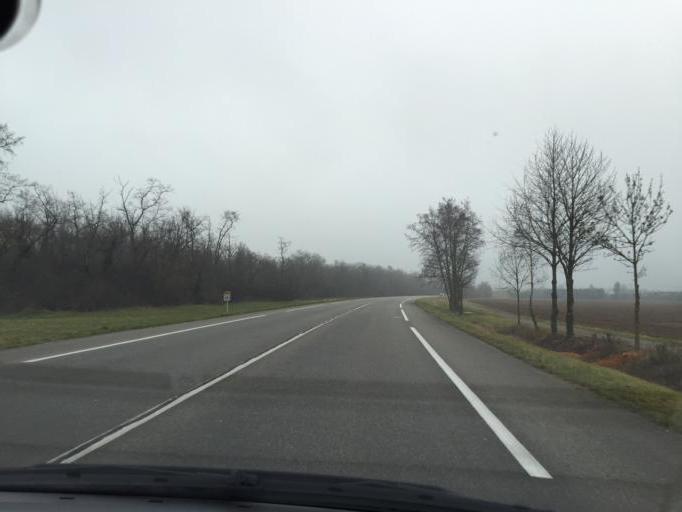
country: FR
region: Alsace
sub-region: Departement du Haut-Rhin
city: Wolfgantzen
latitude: 48.0296
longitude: 7.5110
